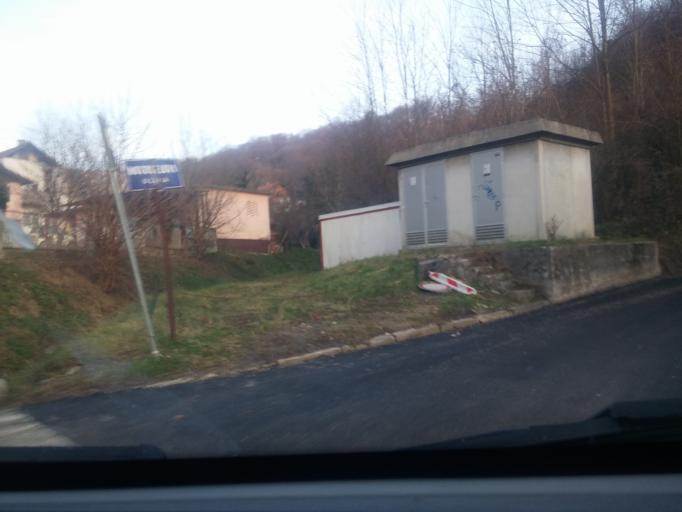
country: HR
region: Grad Zagreb
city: Stenjevec
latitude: 45.8313
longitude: 15.8707
